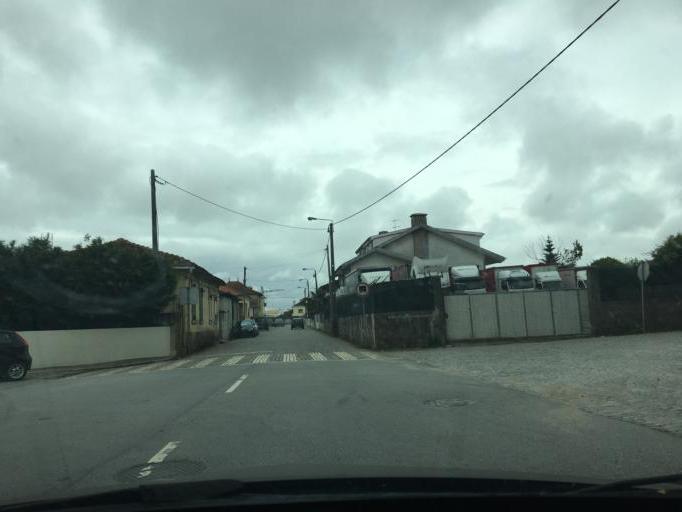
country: PT
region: Porto
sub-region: Matosinhos
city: Santa Cruz do Bispo
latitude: 41.2296
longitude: -8.6597
